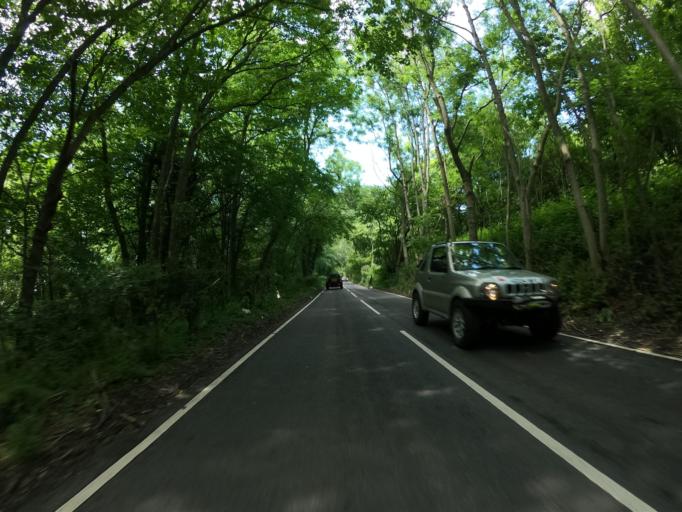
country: GB
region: England
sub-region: Kent
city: Halstead
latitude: 51.3077
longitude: 0.1399
